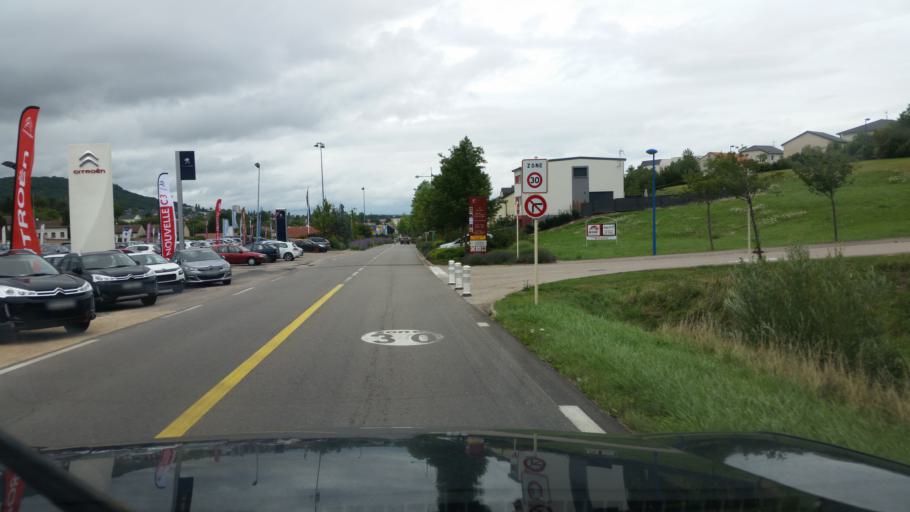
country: FR
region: Lorraine
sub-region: Departement de Meurthe-et-Moselle
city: Toul
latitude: 48.6627
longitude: 5.8788
